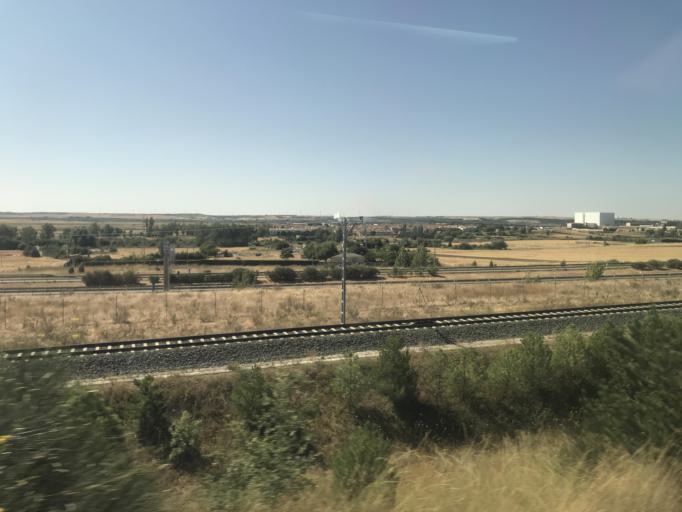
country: ES
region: Castille and Leon
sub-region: Provincia de Burgos
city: Hurones
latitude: 42.3747
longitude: -3.6128
